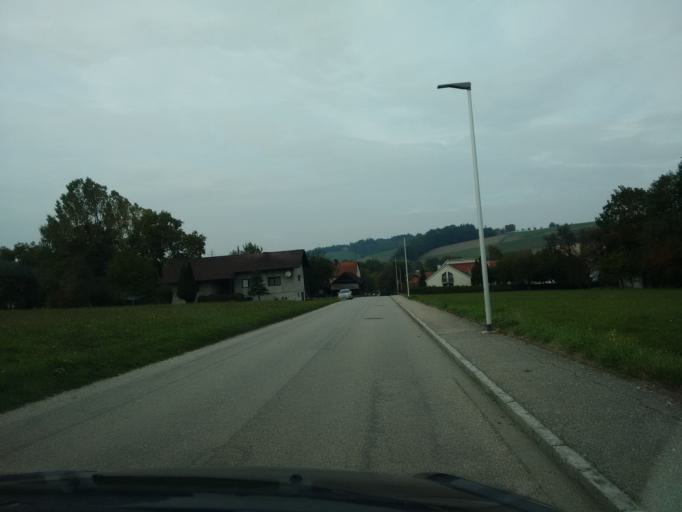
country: AT
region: Upper Austria
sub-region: Wels-Land
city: Offenhausen
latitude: 48.1748
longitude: 13.8596
